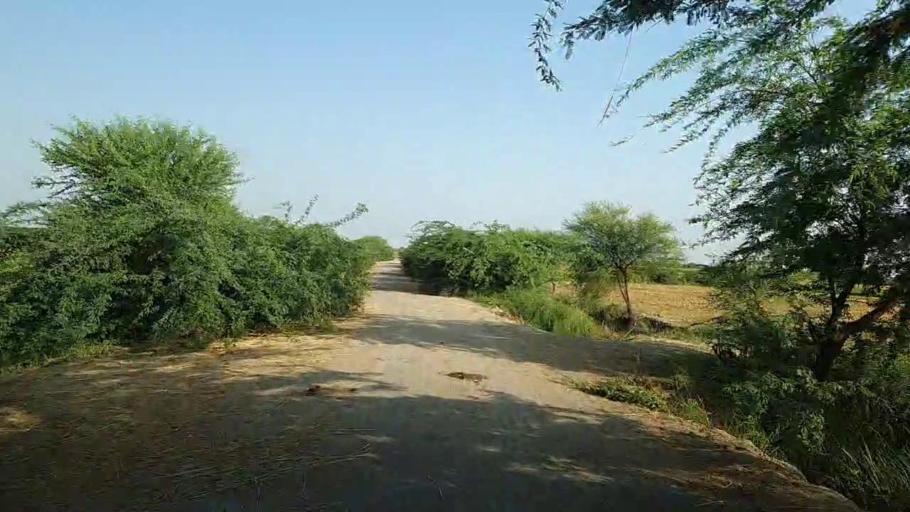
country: PK
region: Sindh
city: Kario
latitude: 24.7767
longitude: 68.6700
